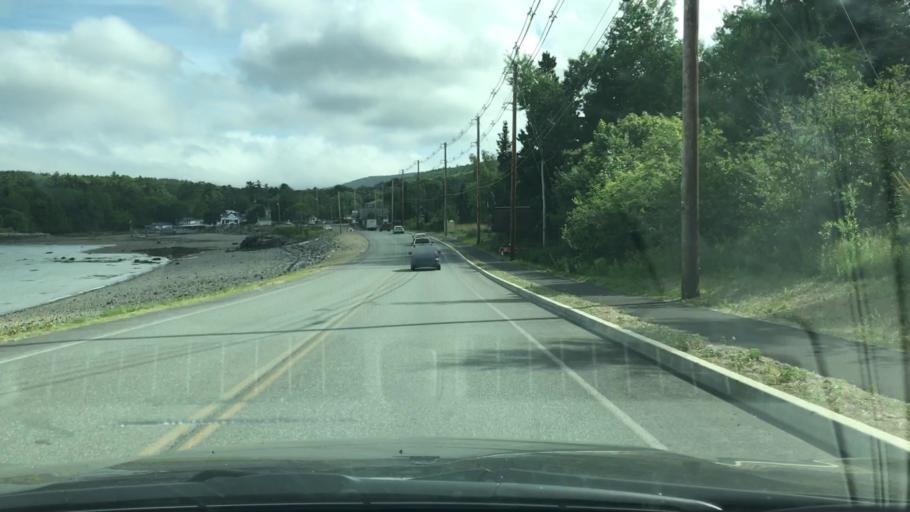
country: US
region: Maine
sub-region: Hancock County
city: Bar Harbor
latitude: 44.4180
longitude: -68.2505
